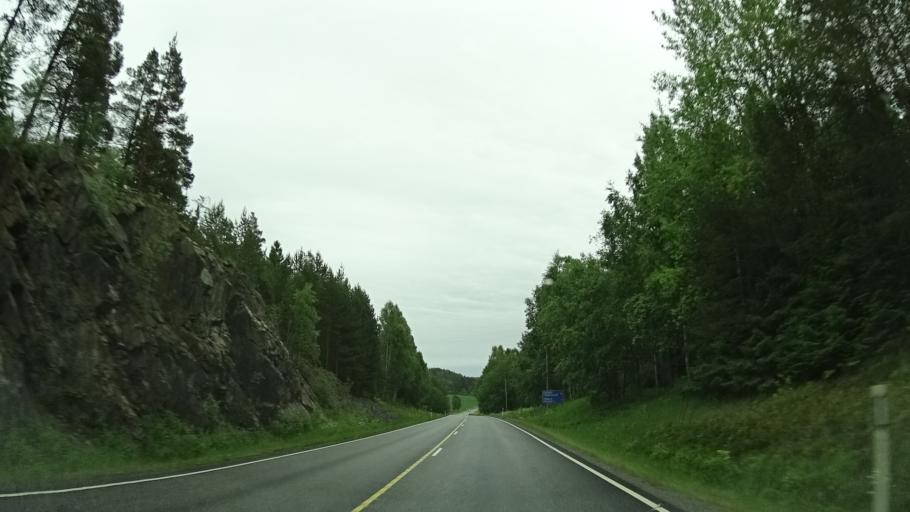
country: FI
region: Varsinais-Suomi
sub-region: Salo
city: Pernioe
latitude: 60.0931
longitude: 23.2230
